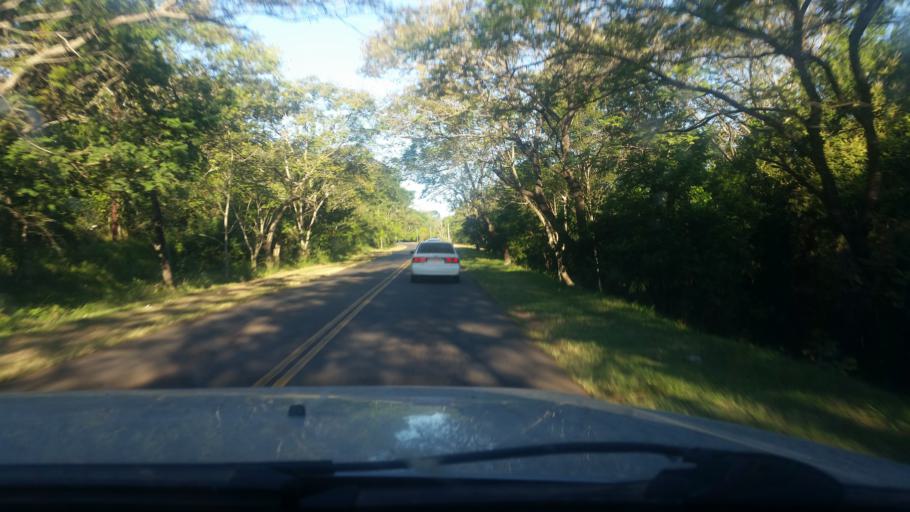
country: PY
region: Guaira
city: Independencia
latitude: -25.7167
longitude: -56.2771
